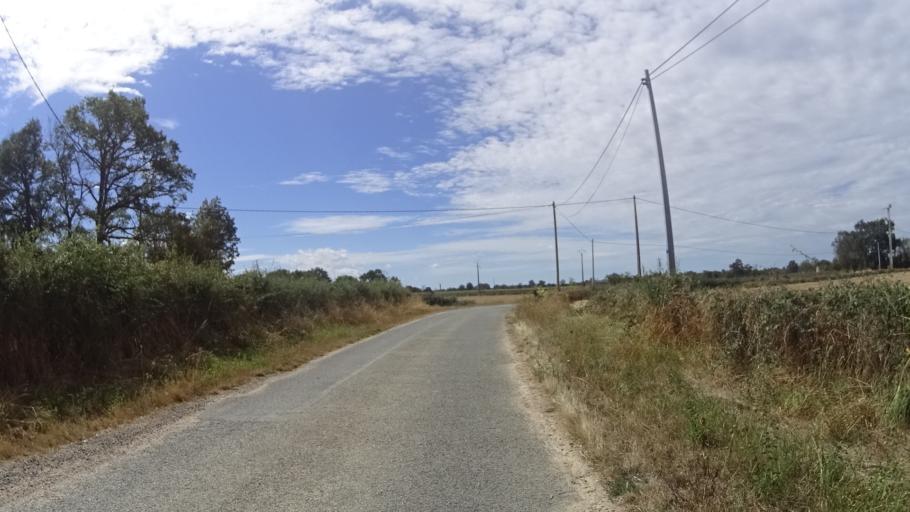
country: FR
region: Auvergne
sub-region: Departement de l'Allier
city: Beaulon
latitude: 46.6492
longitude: 3.6831
